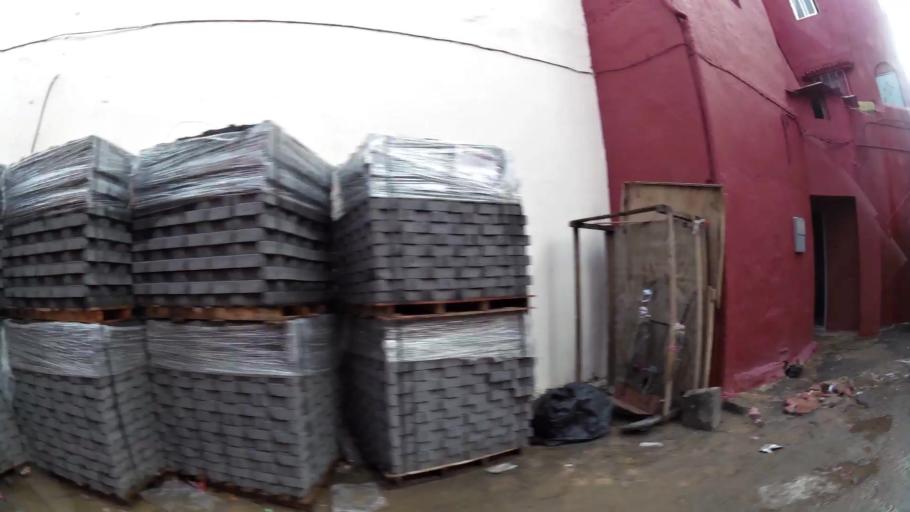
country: MA
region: Grand Casablanca
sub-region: Casablanca
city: Casablanca
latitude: 33.5748
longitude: -7.6022
